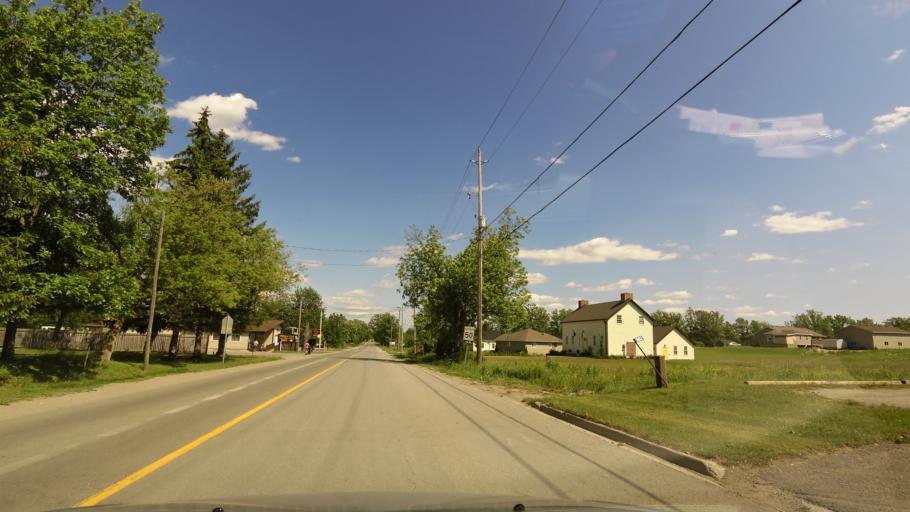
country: CA
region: Ontario
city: Brantford
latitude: 43.0678
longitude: -80.1154
